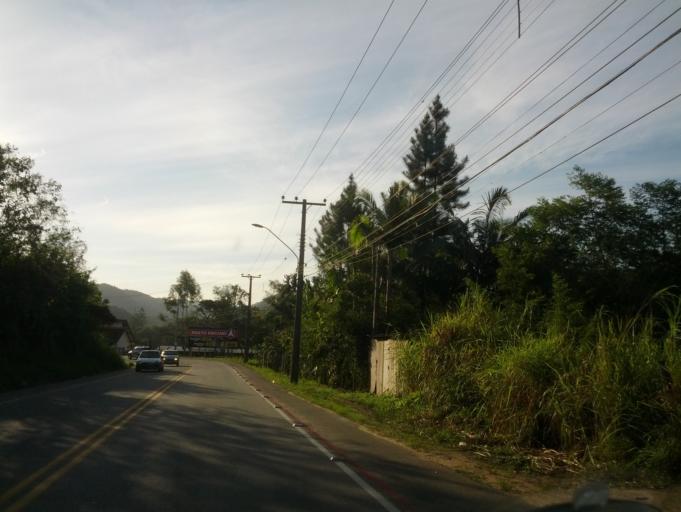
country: BR
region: Santa Catarina
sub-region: Indaial
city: Indaial
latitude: -26.8814
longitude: -49.1757
